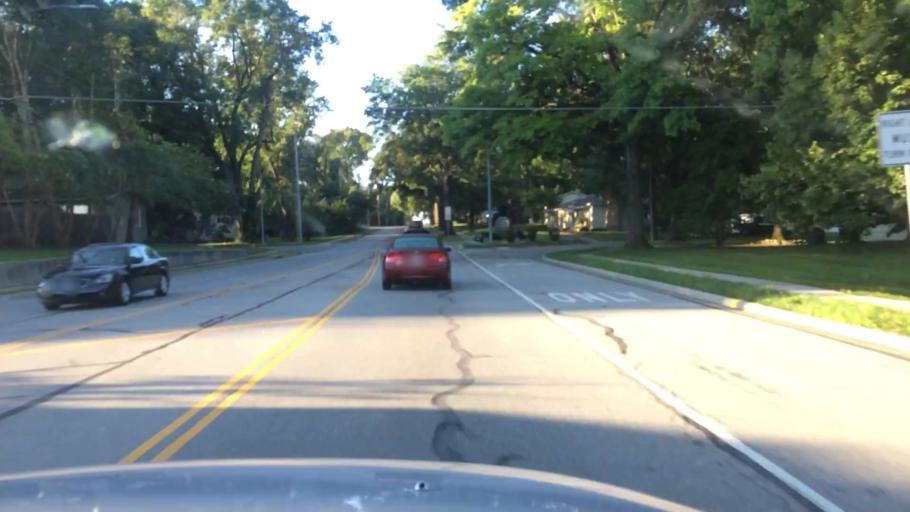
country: US
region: Kansas
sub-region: Johnson County
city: Prairie Village
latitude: 38.9925
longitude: -94.6491
